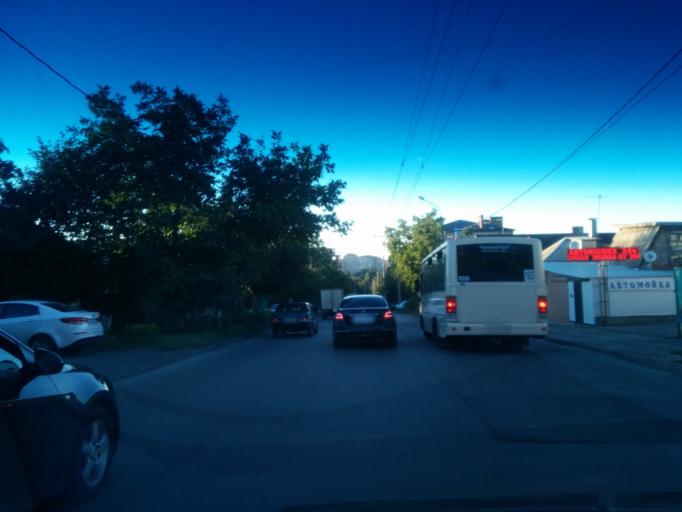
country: RU
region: Rostov
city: Severnyy
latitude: 47.2713
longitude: 39.7208
